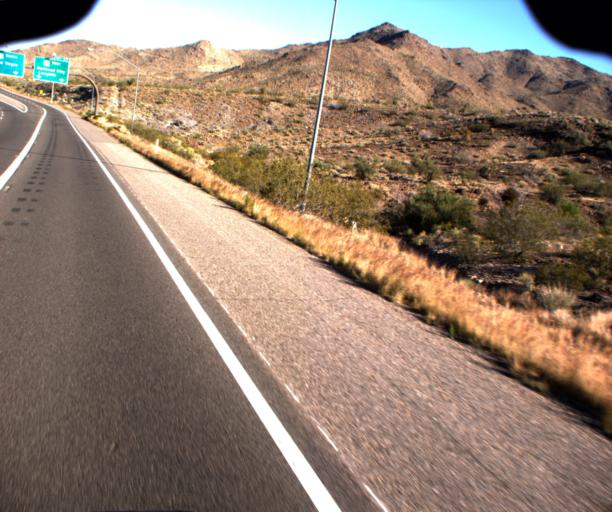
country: US
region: Arizona
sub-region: Mohave County
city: Kingman
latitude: 35.2164
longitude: -114.1161
